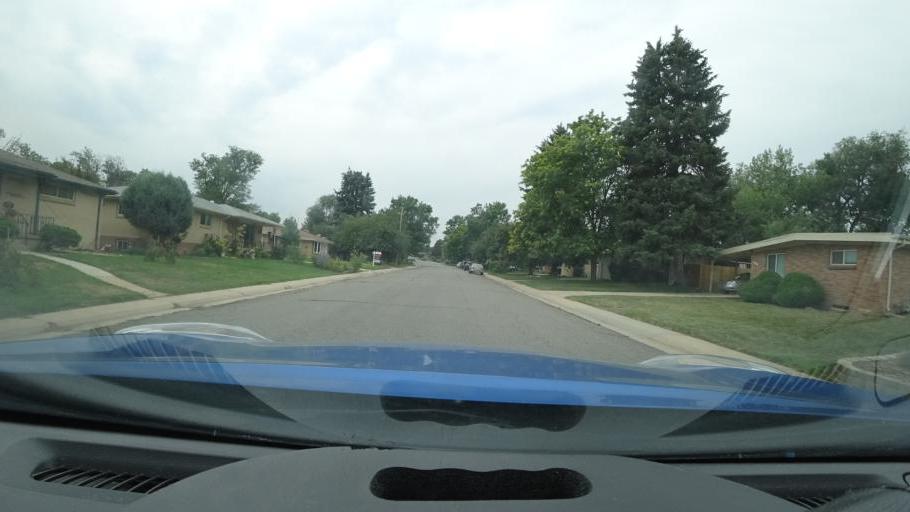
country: US
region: Colorado
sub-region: Arapahoe County
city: Glendale
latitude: 39.6889
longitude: -104.9151
